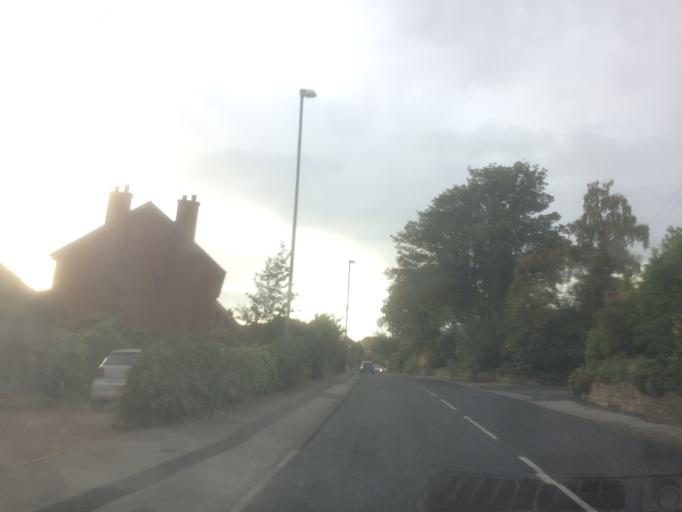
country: GB
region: England
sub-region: City and Borough of Wakefield
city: Pontefract
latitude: 53.7175
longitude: -1.3083
